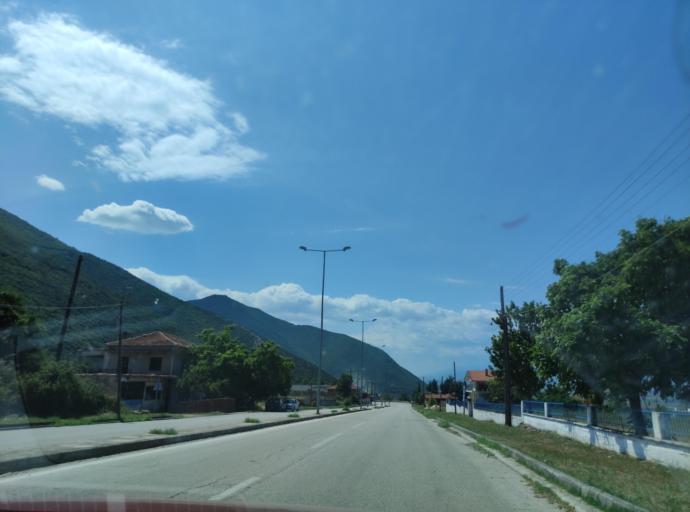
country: GR
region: East Macedonia and Thrace
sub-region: Nomos Kavalas
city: Nikisiani
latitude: 40.9721
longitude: 24.1443
